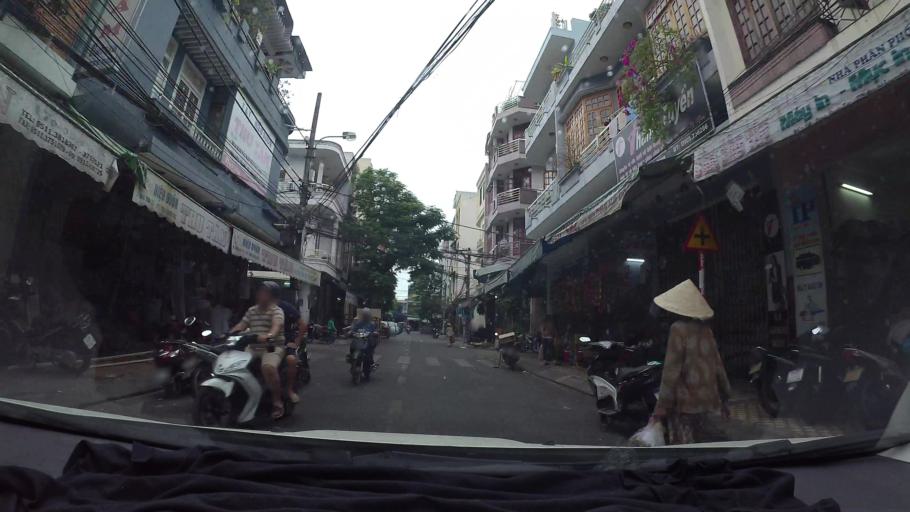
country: VN
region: Da Nang
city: Da Nang
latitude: 16.0681
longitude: 108.2133
